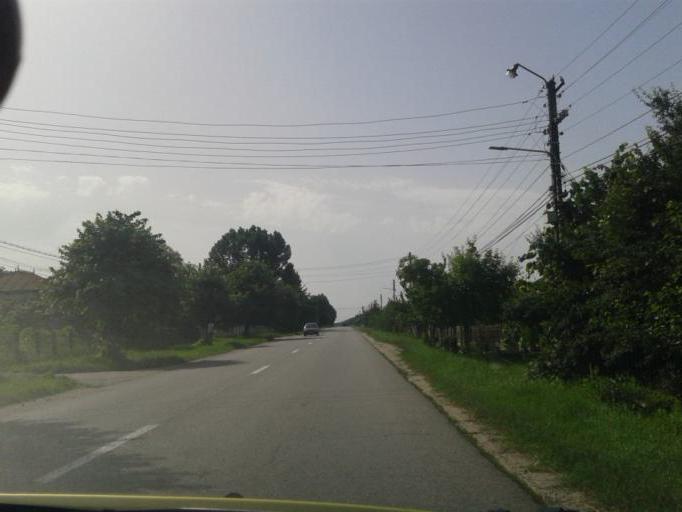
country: RO
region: Valcea
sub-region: Comuna Bunesti
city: Bunesti
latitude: 45.1015
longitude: 24.2052
